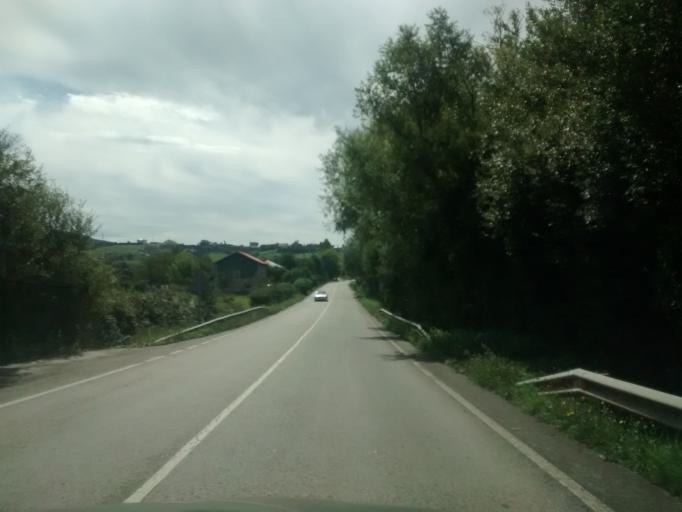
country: ES
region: Cantabria
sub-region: Provincia de Cantabria
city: Miengo
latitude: 43.4179
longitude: -3.9593
